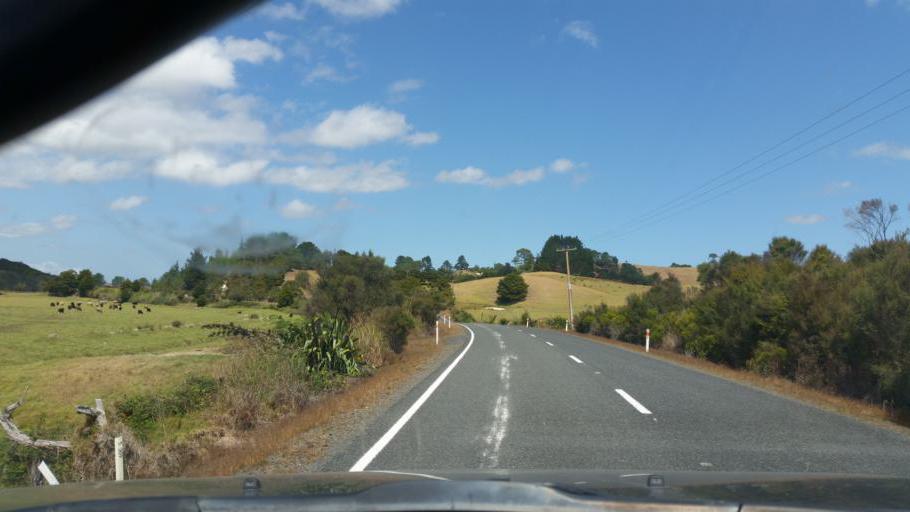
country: NZ
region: Northland
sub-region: Kaipara District
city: Dargaville
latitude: -35.8884
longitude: 173.8411
